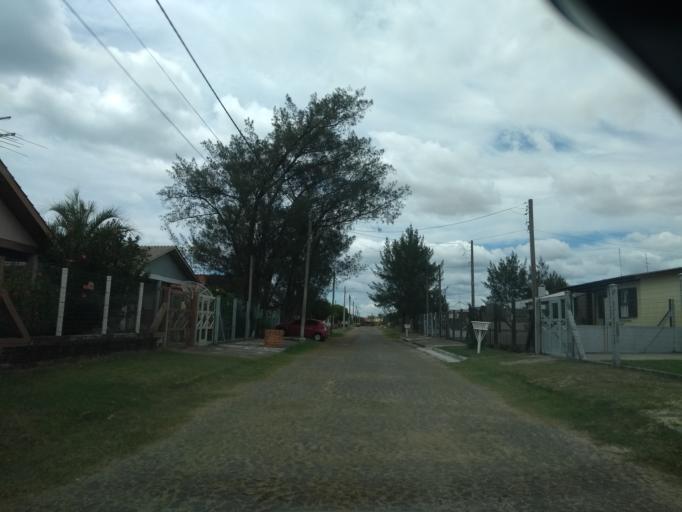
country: BR
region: Rio Grande do Sul
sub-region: Tramandai
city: Tramandai
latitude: -30.0661
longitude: -50.1620
